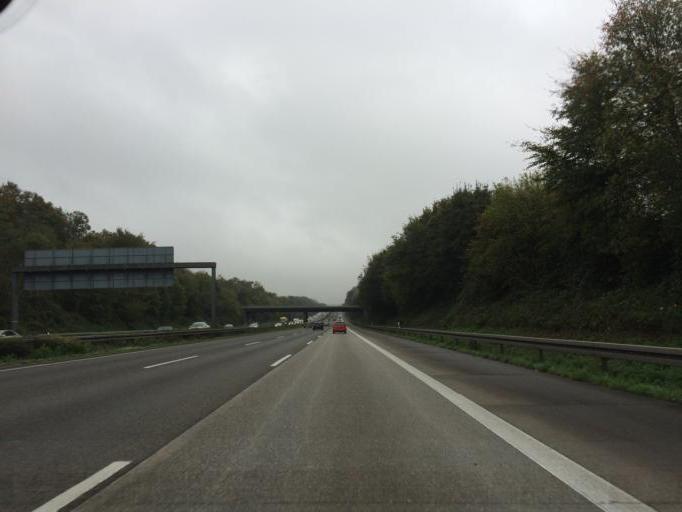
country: DE
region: North Rhine-Westphalia
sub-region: Regierungsbezirk Dusseldorf
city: Ratingen
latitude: 51.3414
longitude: 6.8703
